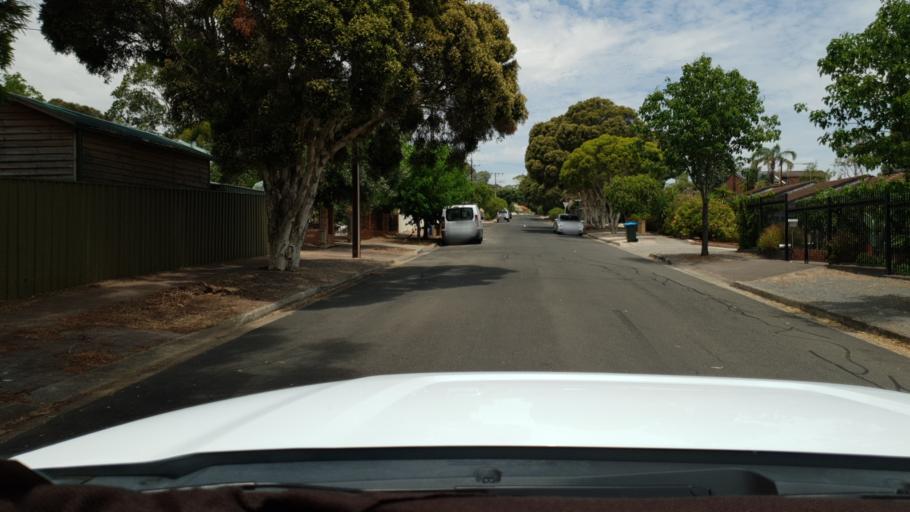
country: AU
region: South Australia
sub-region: Marion
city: Clovelly Park
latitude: -35.0026
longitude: 138.5867
